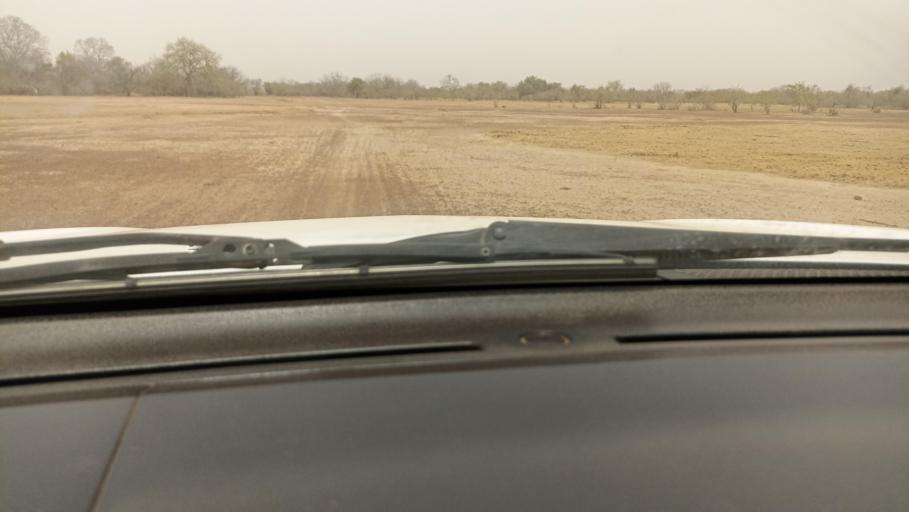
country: BF
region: Boucle du Mouhoun
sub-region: Province du Nayala
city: Toma
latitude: 12.8902
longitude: -2.7821
